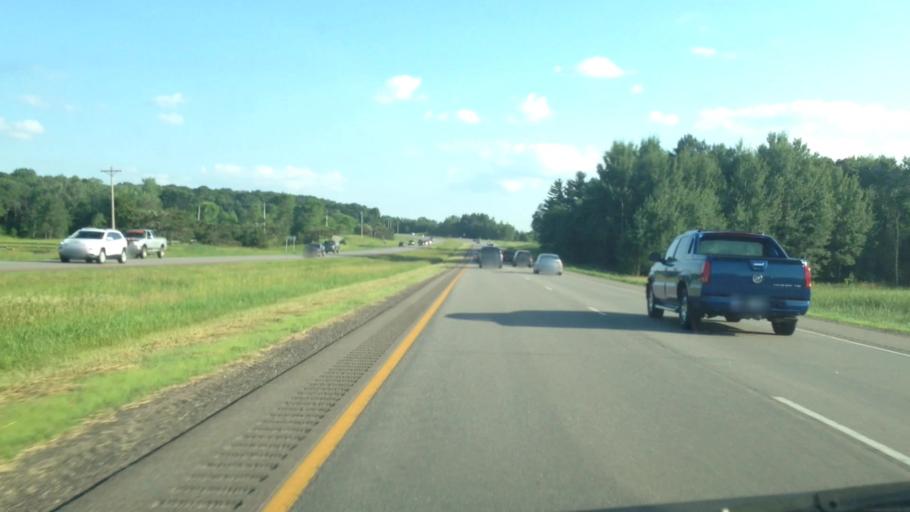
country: US
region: Minnesota
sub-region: Sherburne County
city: Zimmerman
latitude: 45.4095
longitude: -93.5665
